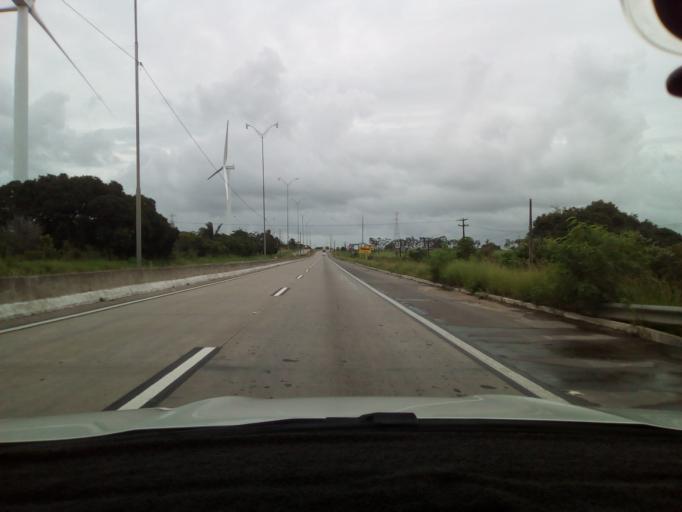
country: BR
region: Paraiba
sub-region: Conde
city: Conde
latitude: -7.2682
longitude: -34.9371
